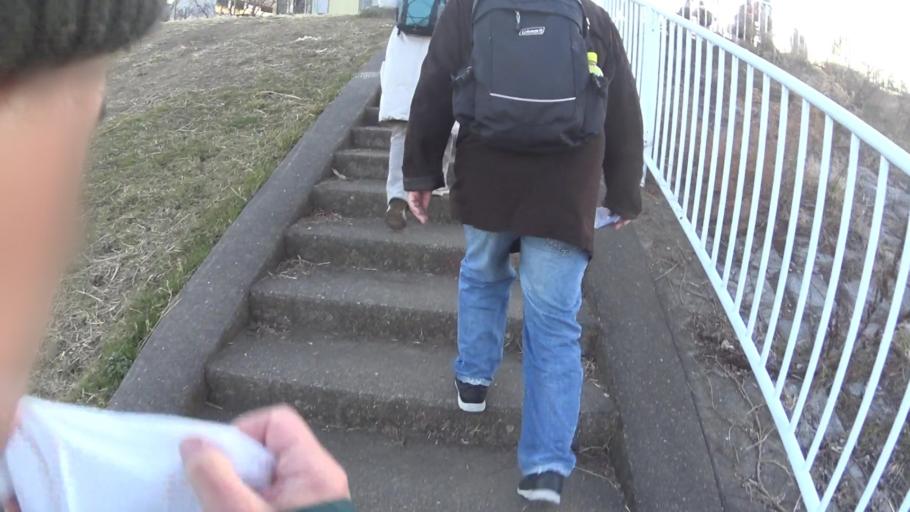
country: JP
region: Saitama
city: Shimotoda
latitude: 35.8486
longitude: 139.6816
